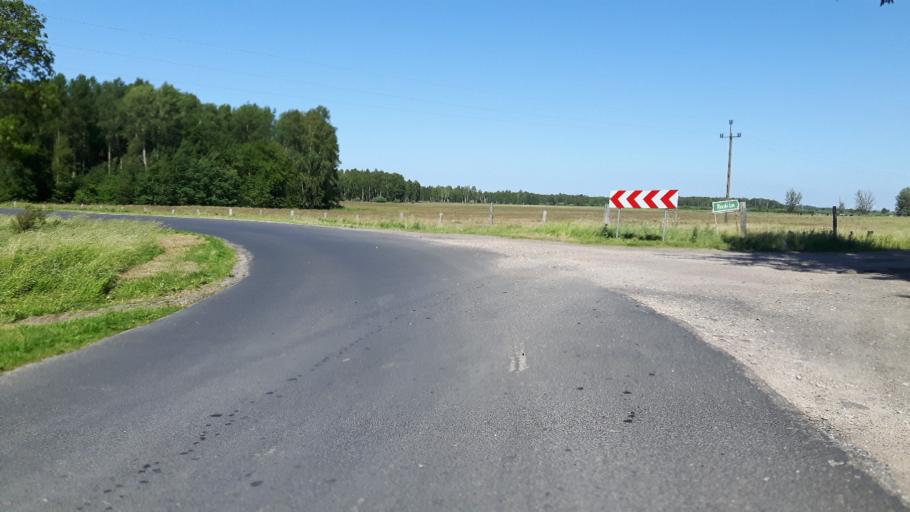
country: PL
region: Pomeranian Voivodeship
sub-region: Powiat slupski
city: Glowczyce
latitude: 54.6420
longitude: 17.4218
